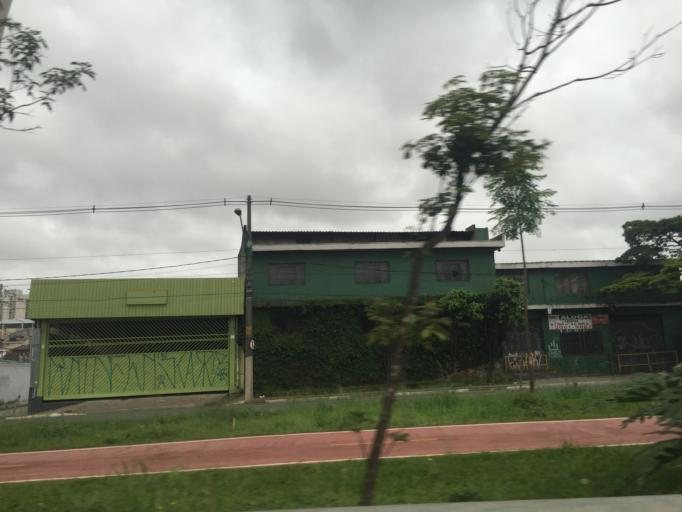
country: BR
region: Sao Paulo
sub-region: Sao Caetano Do Sul
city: Sao Caetano do Sul
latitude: -23.5842
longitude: -46.5769
